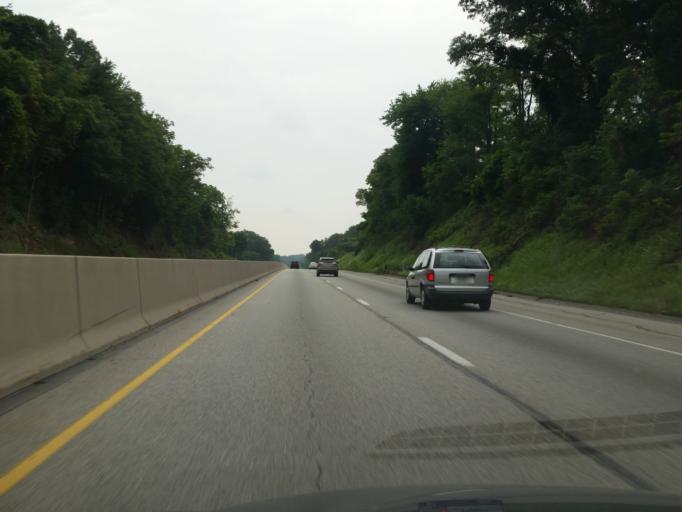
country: US
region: Pennsylvania
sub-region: York County
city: Manchester
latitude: 40.0919
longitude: -76.7712
